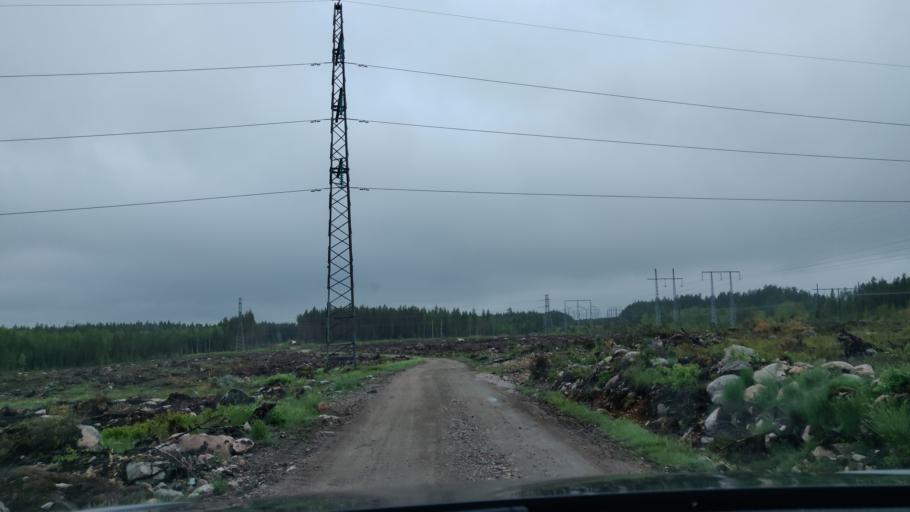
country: SE
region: Dalarna
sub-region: Avesta Kommun
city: Horndal
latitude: 60.3128
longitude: 16.4005
